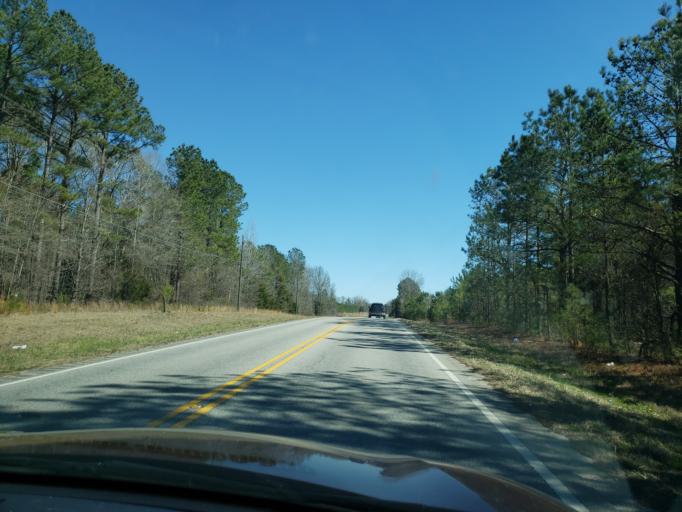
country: US
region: Alabama
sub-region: Lee County
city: Auburn
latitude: 32.5989
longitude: -85.5747
